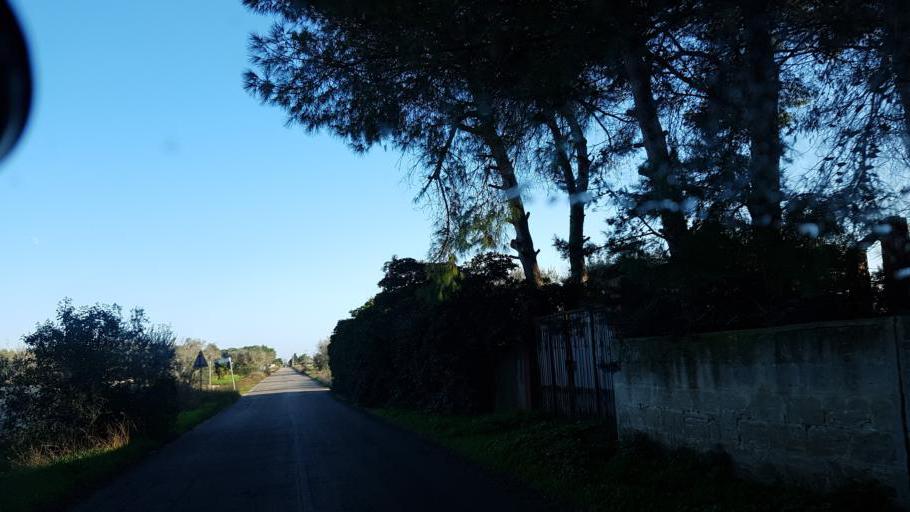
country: IT
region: Apulia
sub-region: Provincia di Brindisi
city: Torchiarolo
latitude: 40.5076
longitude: 18.0935
